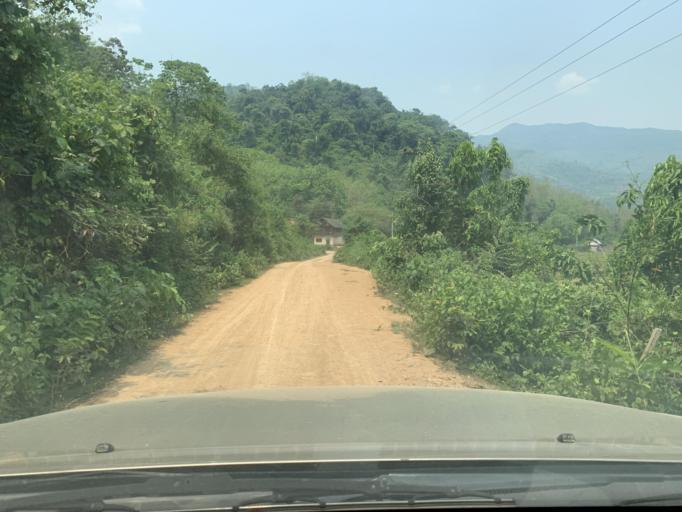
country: LA
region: Louangphabang
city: Louangphabang
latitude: 19.9695
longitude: 102.1256
